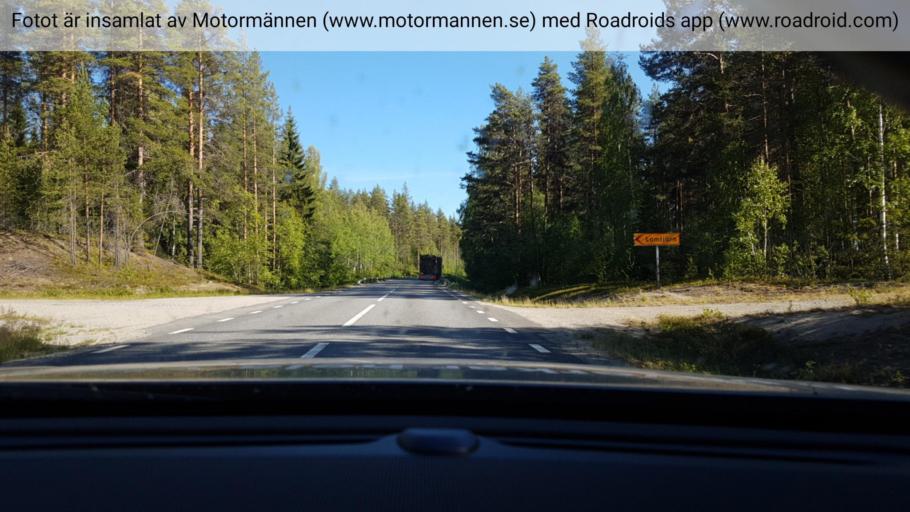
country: SE
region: Vaesterbotten
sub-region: Bjurholms Kommun
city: Bjurholm
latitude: 64.3496
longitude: 19.1477
